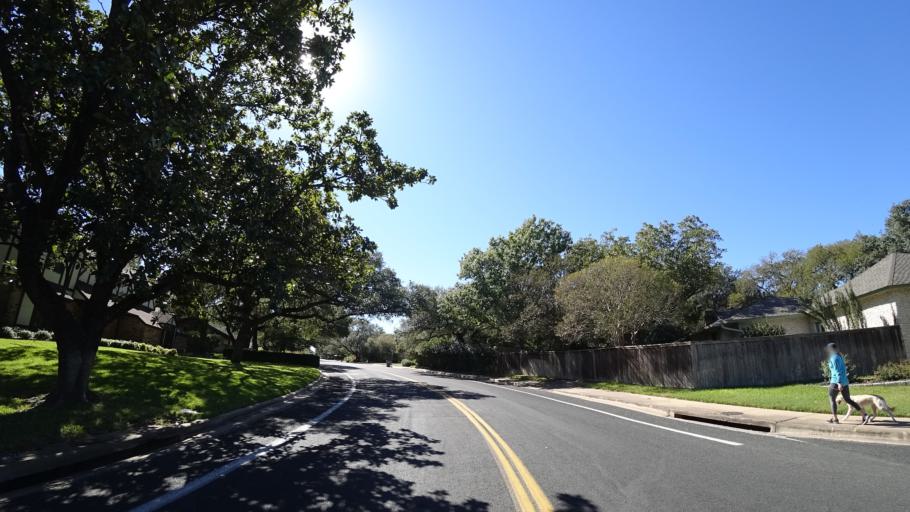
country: US
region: Texas
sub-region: Travis County
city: West Lake Hills
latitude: 30.3604
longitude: -97.7590
